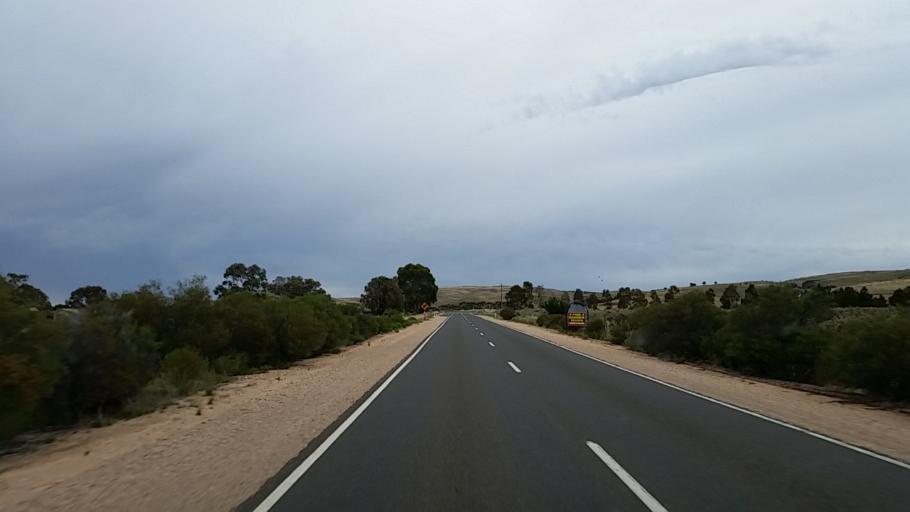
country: AU
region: South Australia
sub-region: Mid Murray
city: Mannum
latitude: -34.7589
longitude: 139.2148
